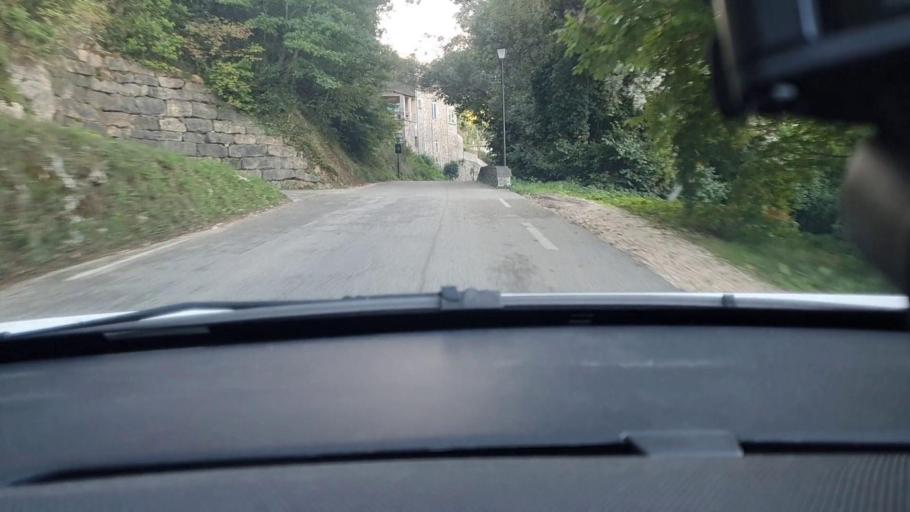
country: FR
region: Languedoc-Roussillon
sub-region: Departement du Gard
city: Barjac
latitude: 44.2381
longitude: 4.2942
